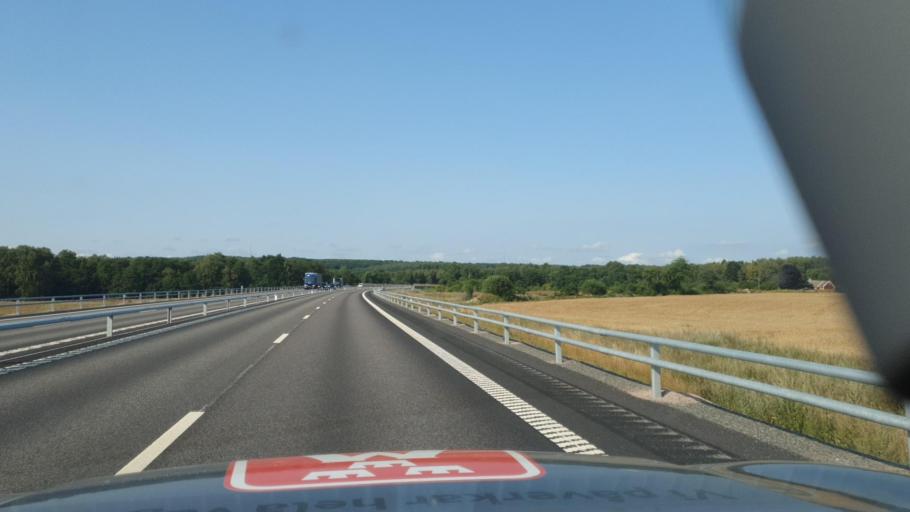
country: SE
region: Skane
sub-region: Kristianstads Kommun
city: Onnestad
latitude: 55.9541
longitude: 13.9199
